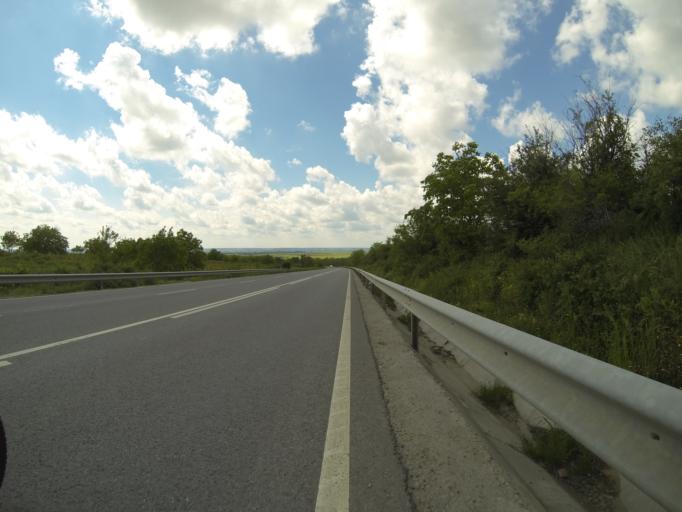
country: RO
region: Dolj
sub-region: Comuna Carcea
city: Carcea
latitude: 44.2655
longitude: 23.8943
